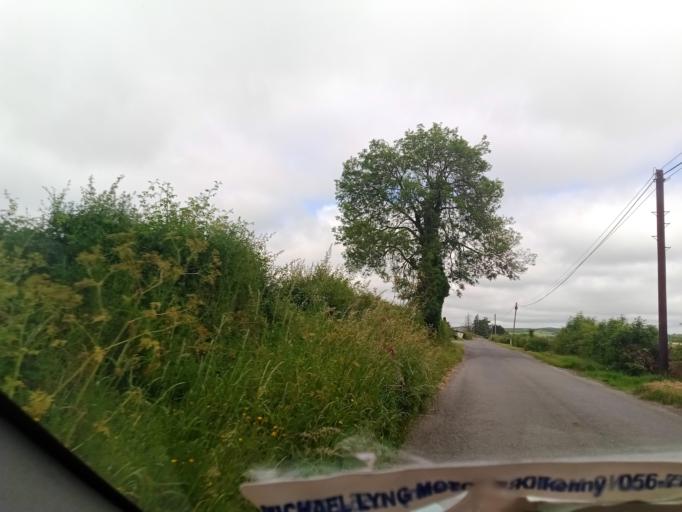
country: IE
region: Leinster
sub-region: Kilkenny
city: Ballyragget
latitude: 52.7553
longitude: -7.4458
